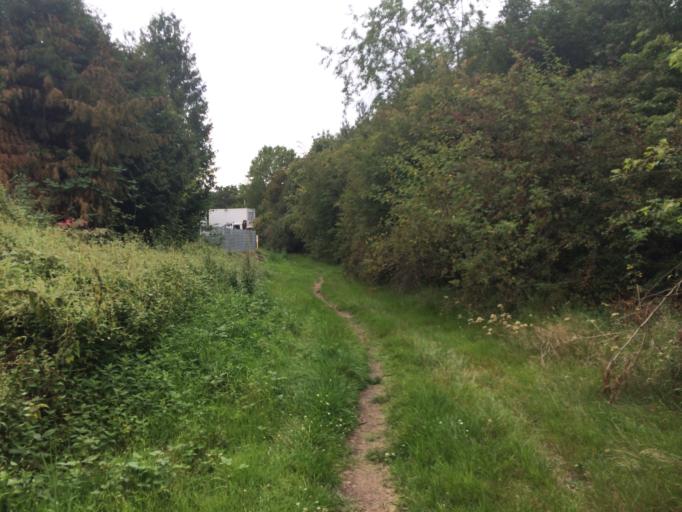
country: DE
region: Hesse
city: Morfelden-Walldorf
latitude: 50.0167
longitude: 8.5814
